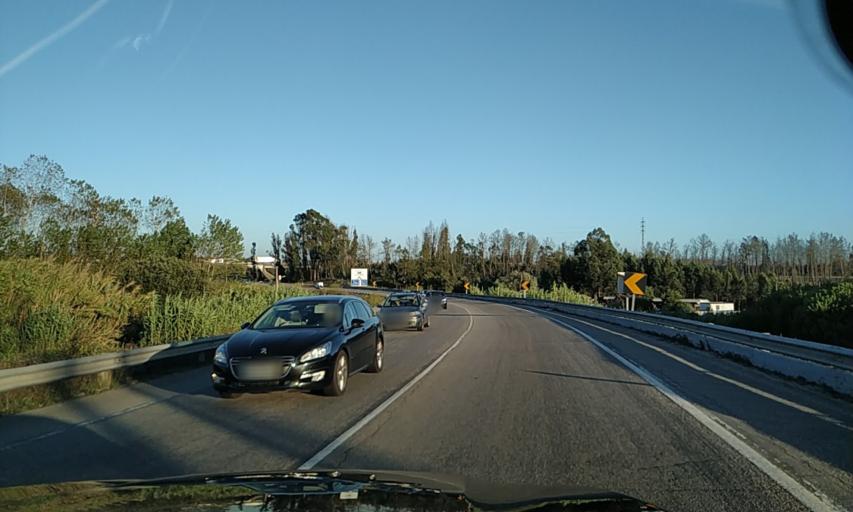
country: PT
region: Aveiro
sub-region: Aveiro
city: Oliveirinha
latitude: 40.5852
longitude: -8.6061
